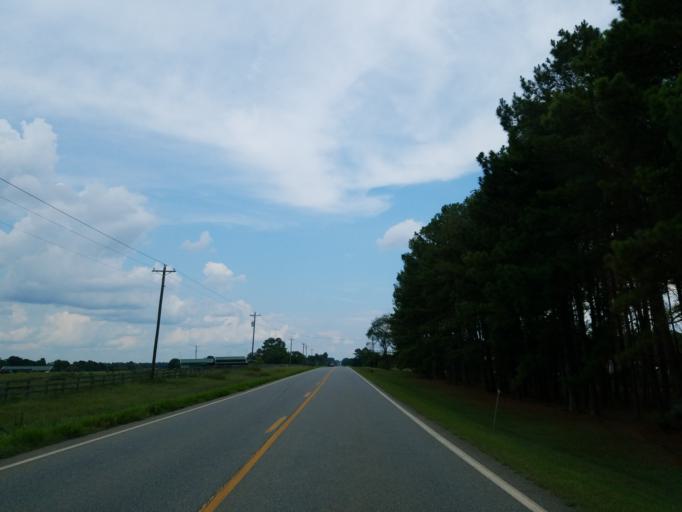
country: US
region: Georgia
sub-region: Dooly County
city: Unadilla
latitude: 32.3333
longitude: -83.7553
